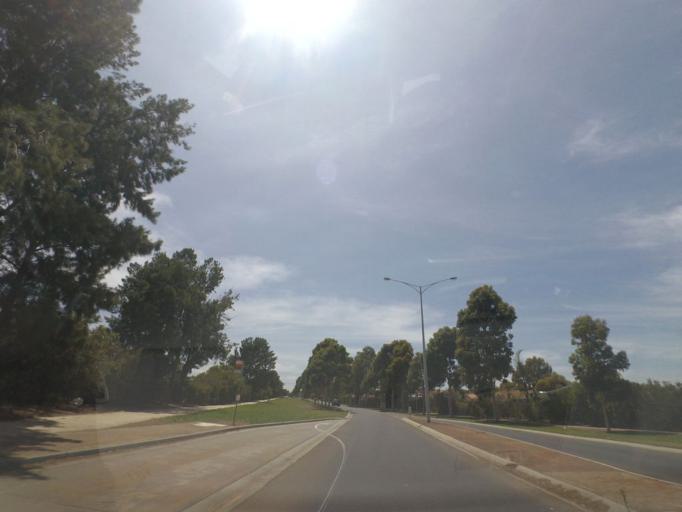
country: AU
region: Victoria
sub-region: Hume
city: Roxburgh Park
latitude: -37.6296
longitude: 144.9200
